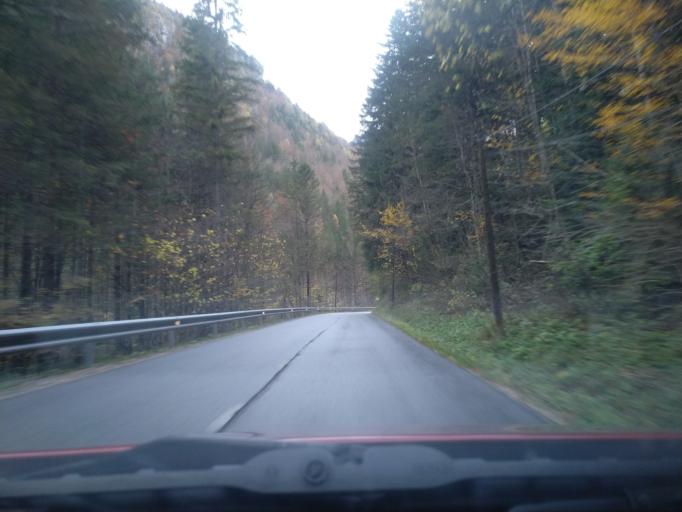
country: SI
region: Luce
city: Luce
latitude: 46.3682
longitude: 14.7308
